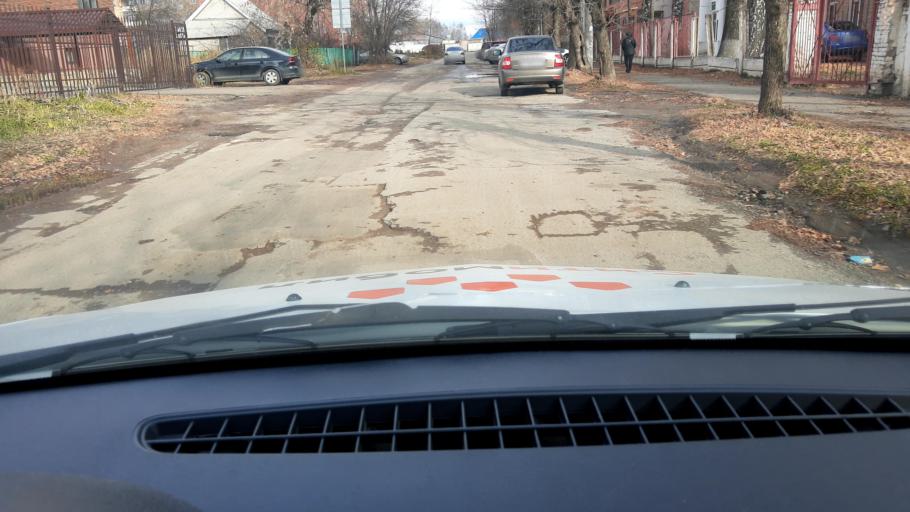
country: RU
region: Bashkortostan
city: Ufa
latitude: 54.8205
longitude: 56.1044
